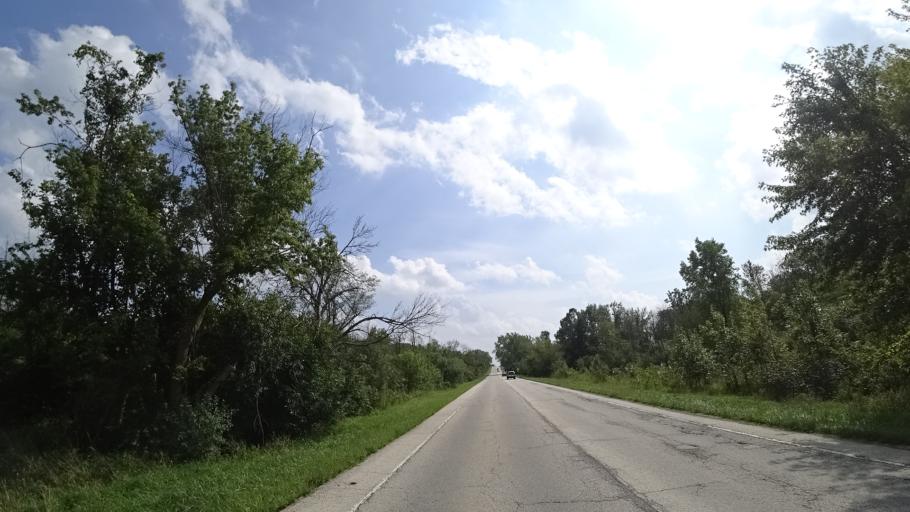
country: US
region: Illinois
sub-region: Will County
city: Goodings Grove
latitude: 41.6464
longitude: -87.9120
